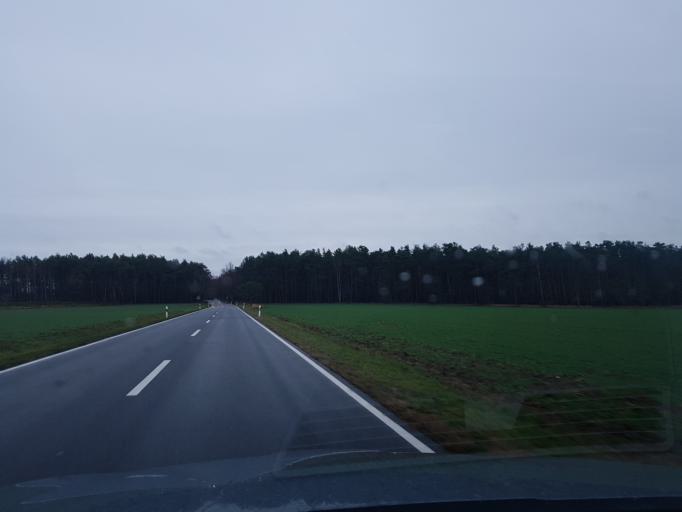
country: DE
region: Brandenburg
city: Finsterwalde
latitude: 51.6555
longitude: 13.6915
